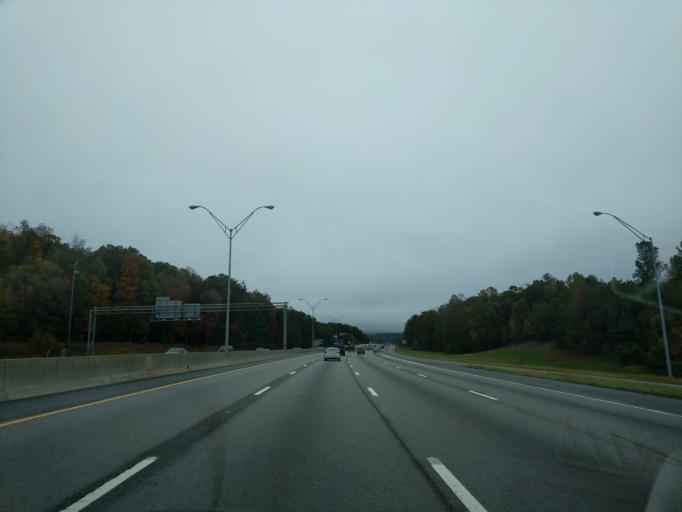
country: US
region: North Carolina
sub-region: Orange County
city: Hillsborough
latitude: 36.0725
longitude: -79.1592
